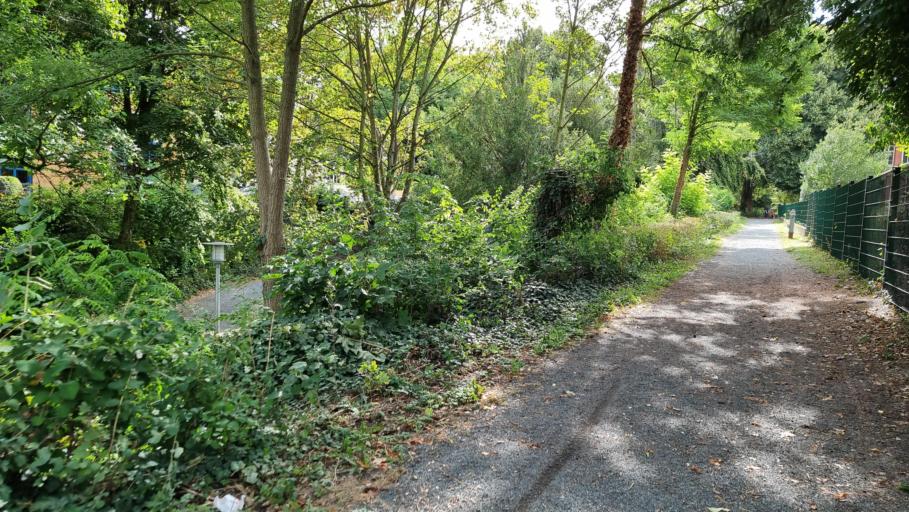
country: DE
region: Lower Saxony
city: Alfeld
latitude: 51.9885
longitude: 9.8270
